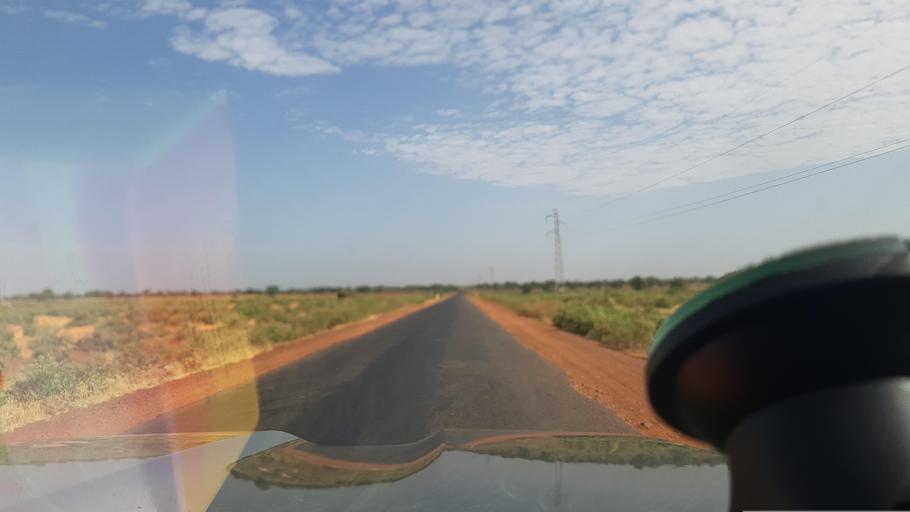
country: ML
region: Segou
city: Segou
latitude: 13.5486
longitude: -6.1181
